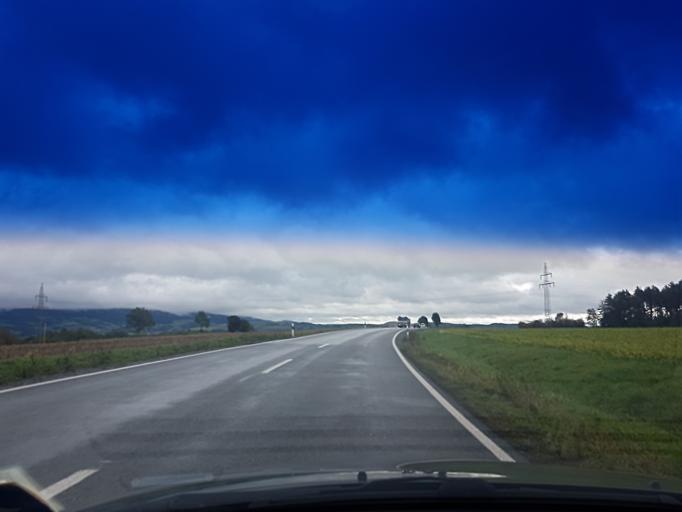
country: DE
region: Bavaria
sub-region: Upper Franconia
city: Bindlach
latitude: 50.0142
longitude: 11.6103
